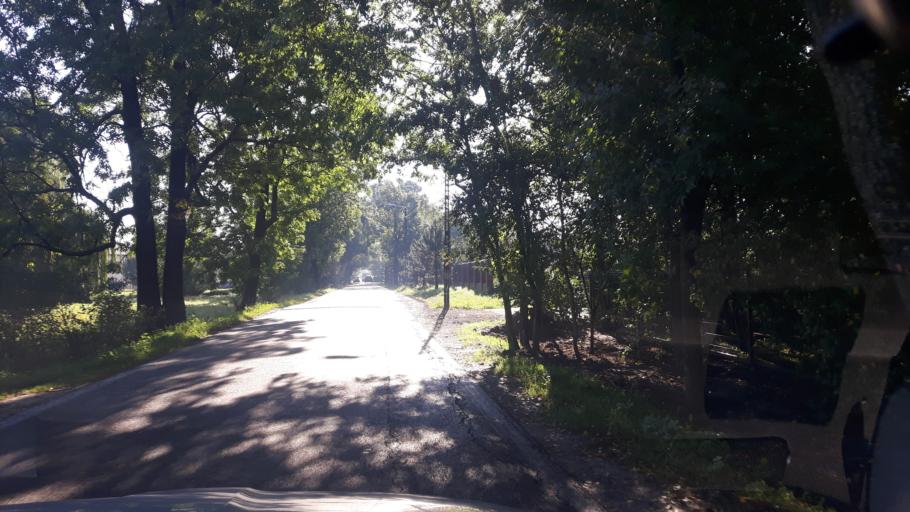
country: PL
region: Masovian Voivodeship
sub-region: Powiat legionowski
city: Stanislawow Pierwszy
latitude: 52.3515
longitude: 21.0222
